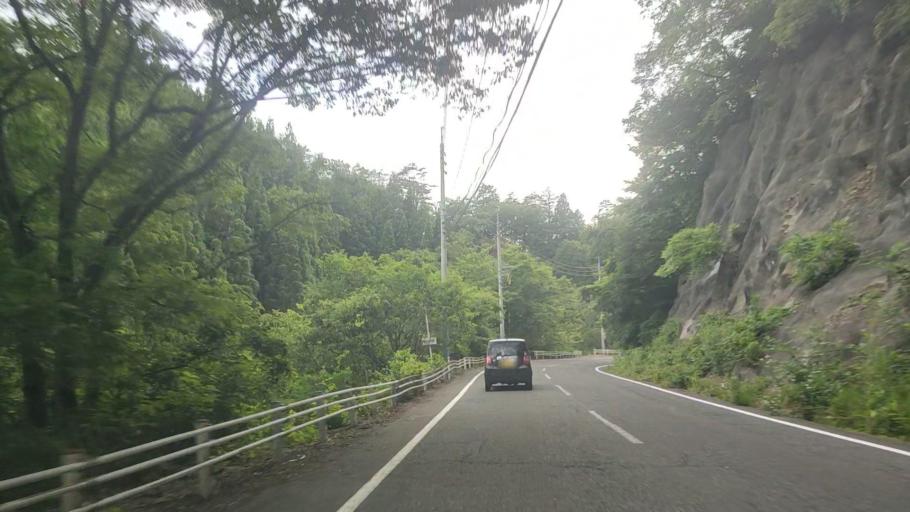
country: JP
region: Tottori
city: Kurayoshi
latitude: 35.2954
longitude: 133.9518
